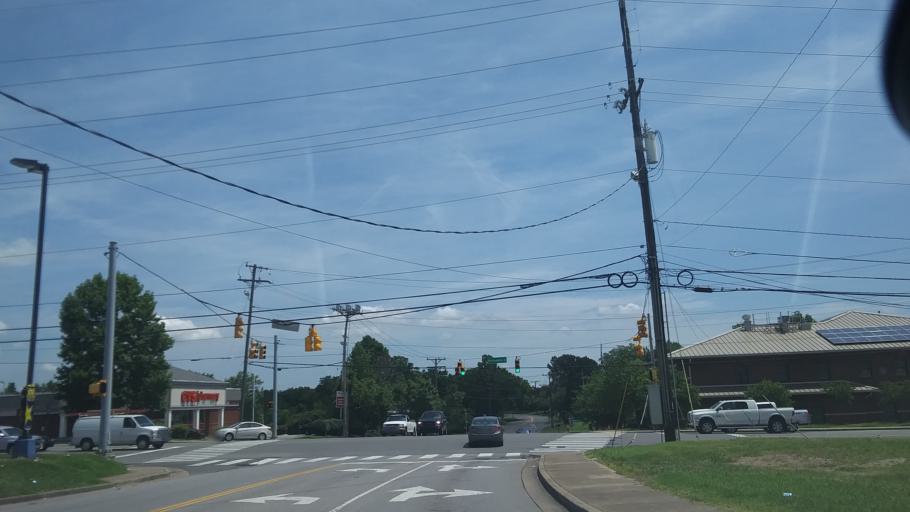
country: US
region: Tennessee
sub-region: Rutherford County
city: La Vergne
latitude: 36.0671
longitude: -86.6316
